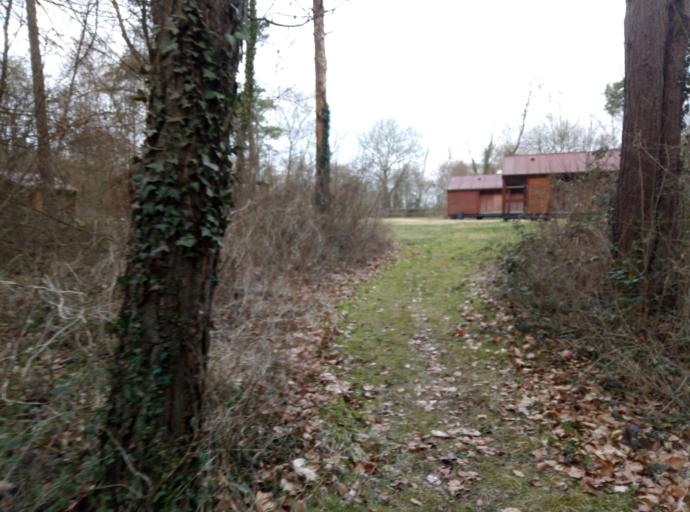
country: FR
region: Picardie
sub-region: Departement de l'Aisne
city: Vic-sur-Aisne
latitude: 49.4382
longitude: 3.1283
